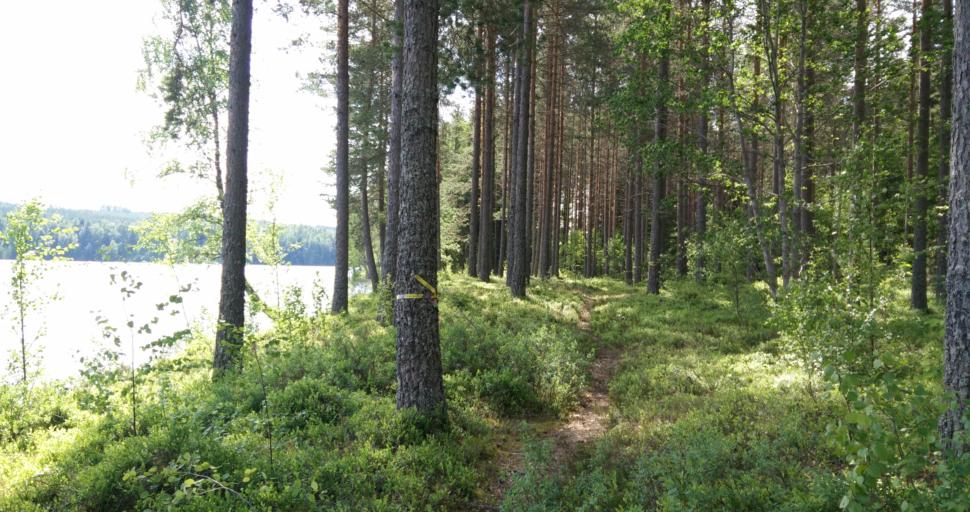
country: SE
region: Vaermland
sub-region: Hagfors Kommun
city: Hagfors
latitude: 59.9952
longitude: 13.5708
